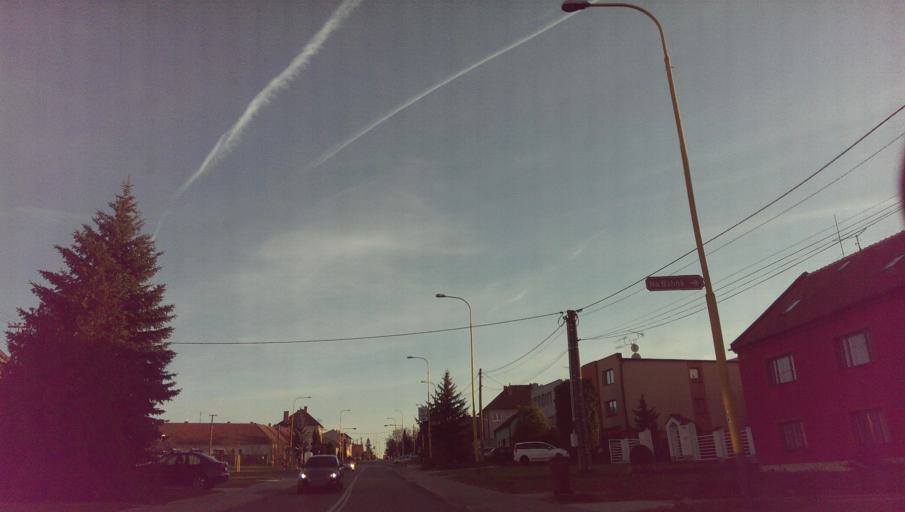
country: CZ
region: Zlin
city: Kunovice
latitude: 49.0629
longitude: 17.4819
